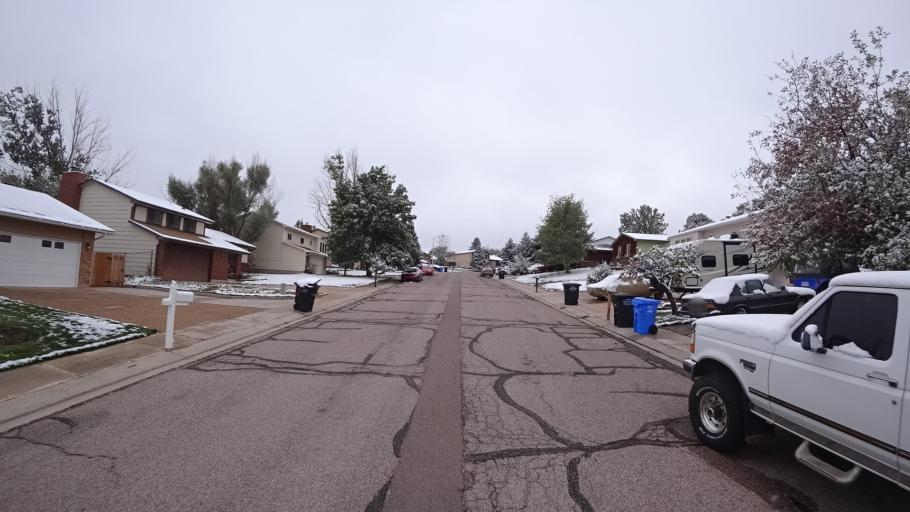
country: US
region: Colorado
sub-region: El Paso County
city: Cimarron Hills
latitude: 38.9227
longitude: -104.7654
